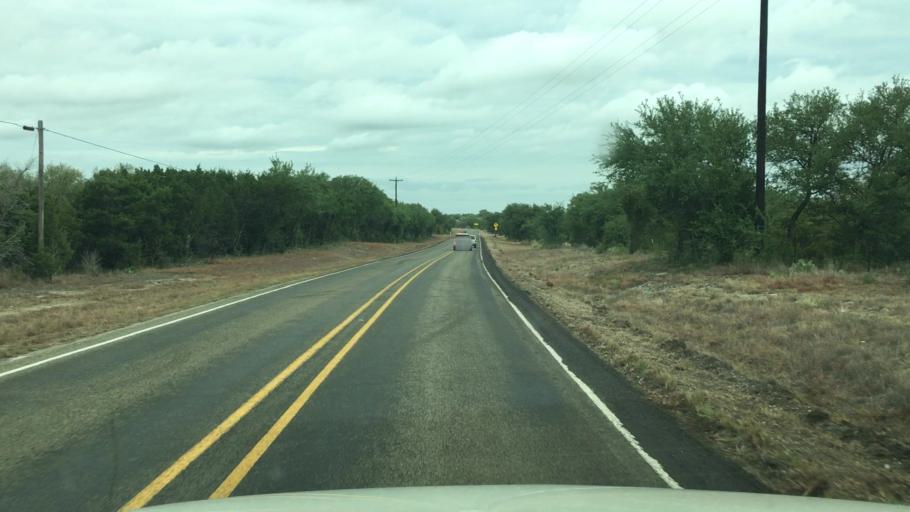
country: US
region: Texas
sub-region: Llano County
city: Horseshoe Bay
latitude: 30.4730
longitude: -98.4157
